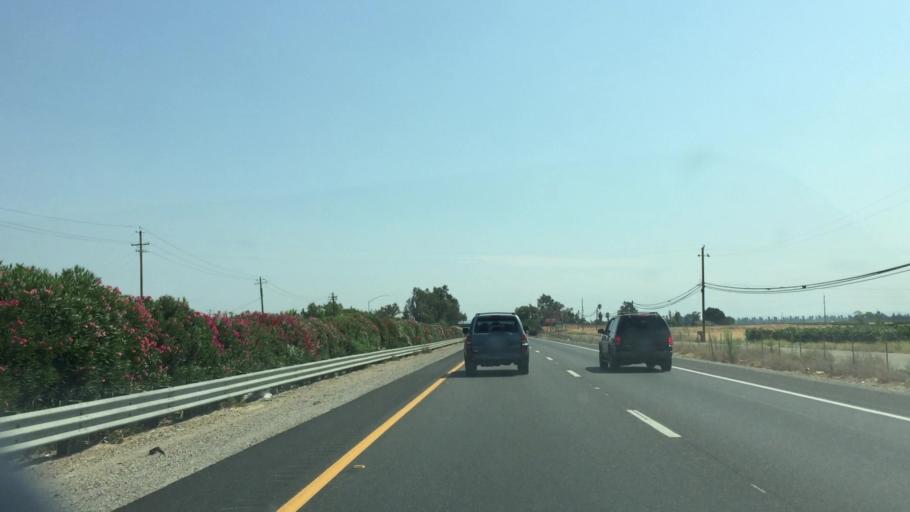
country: US
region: California
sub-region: San Joaquin County
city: Collierville
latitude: 38.1936
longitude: -121.2629
